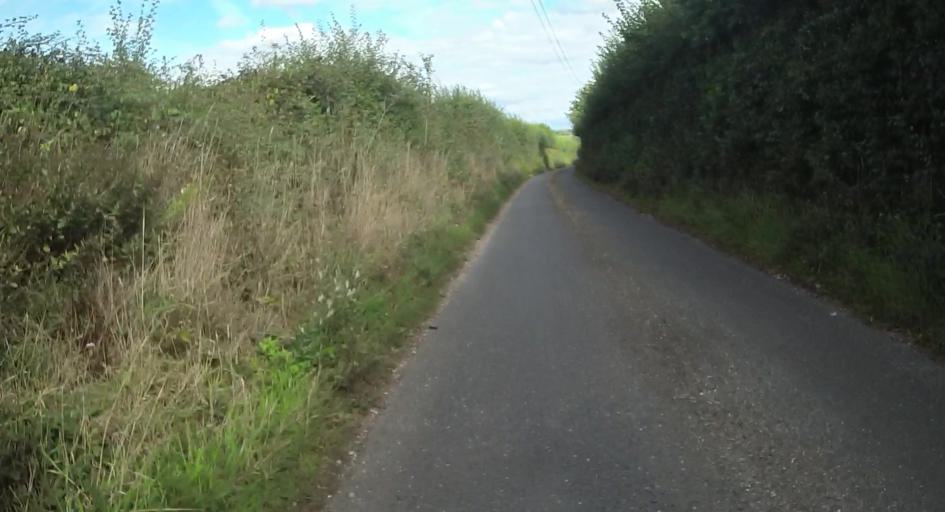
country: GB
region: England
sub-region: West Berkshire
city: Thatcham
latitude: 51.3739
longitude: -1.2140
